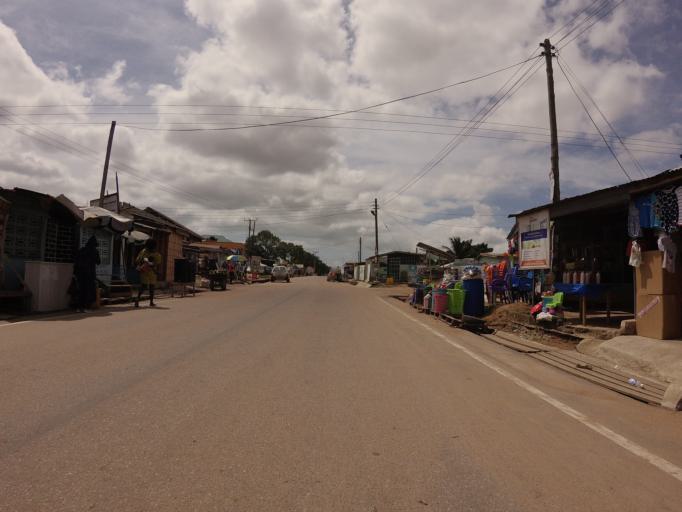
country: GH
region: Central
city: Kasoa
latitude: 5.5376
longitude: -0.4010
